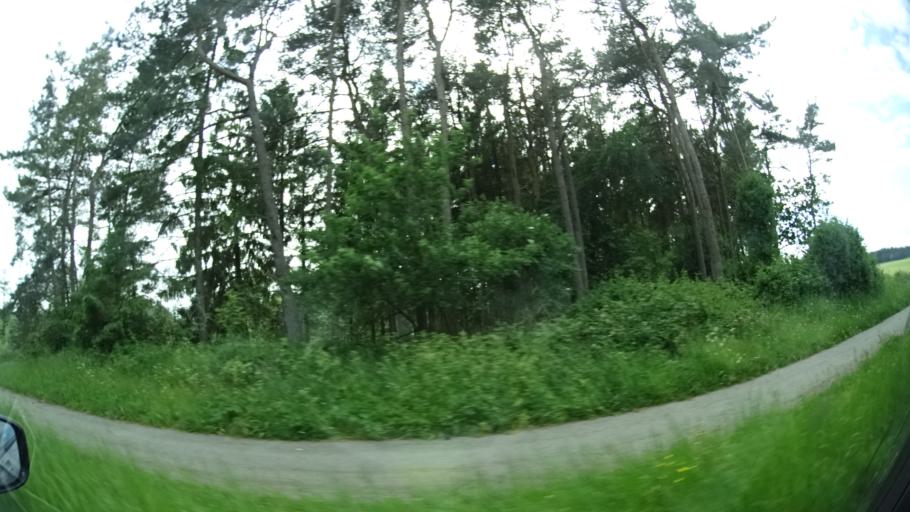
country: DK
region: Central Jutland
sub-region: Norddjurs Kommune
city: Grenaa
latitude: 56.5043
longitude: 10.7355
